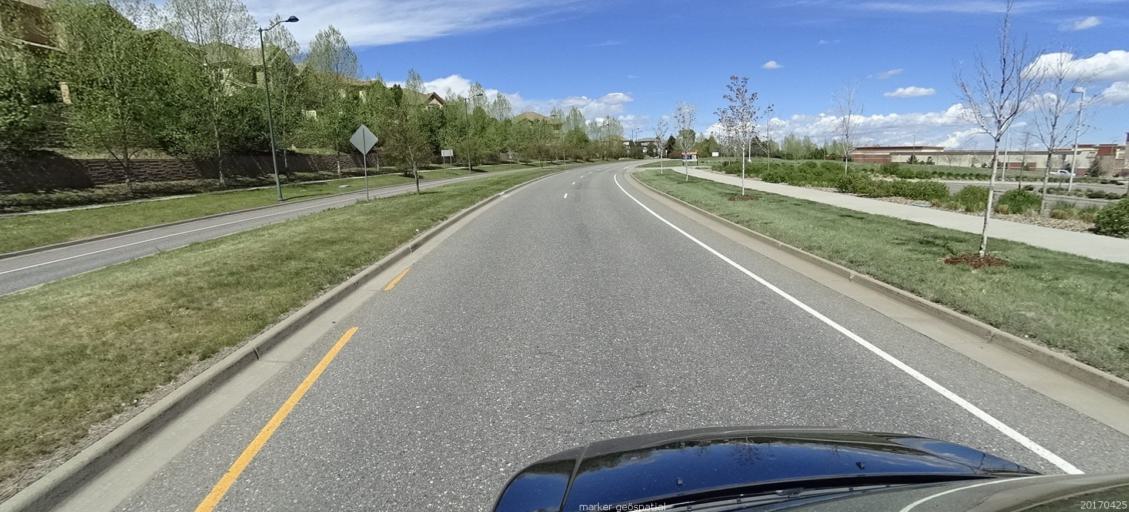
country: US
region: Colorado
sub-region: Douglas County
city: Carriage Club
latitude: 39.5322
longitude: -104.8836
